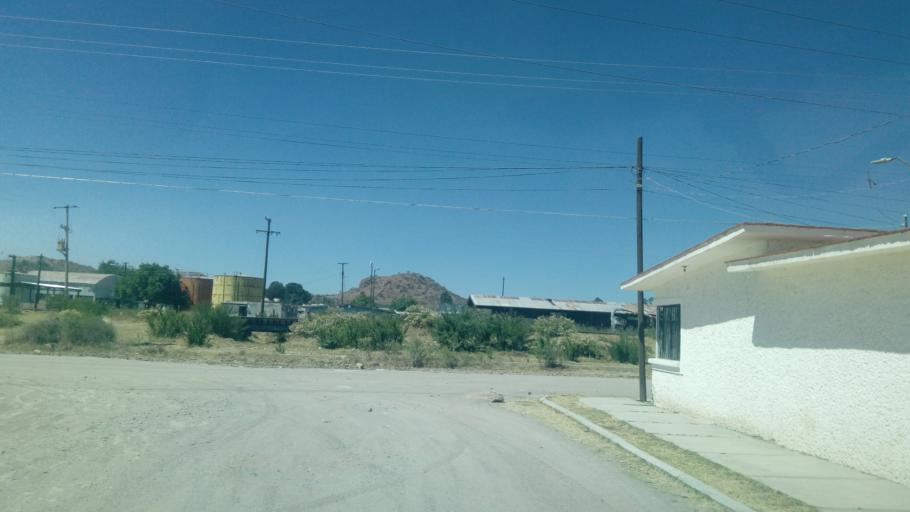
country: MX
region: Durango
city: Victoria de Durango
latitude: 24.0777
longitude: -104.6593
